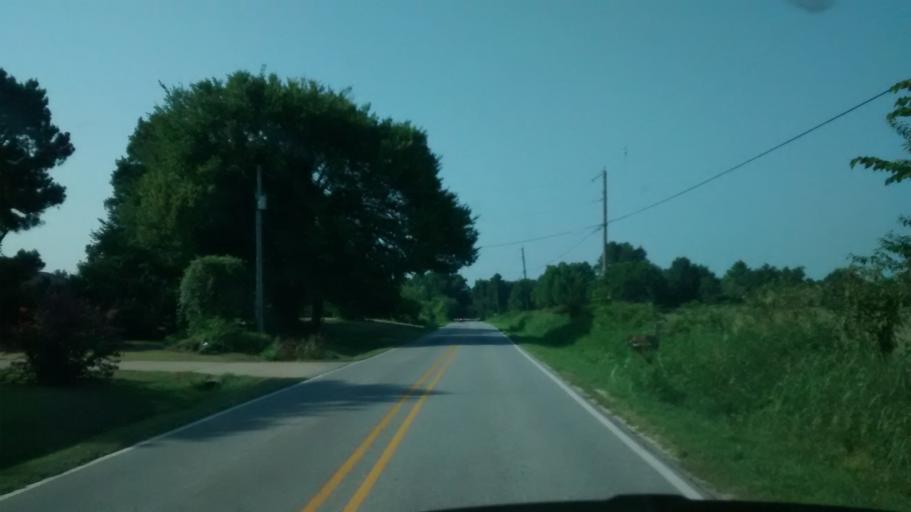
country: US
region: Arkansas
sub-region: Washington County
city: Farmington
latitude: 36.0644
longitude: -94.2535
